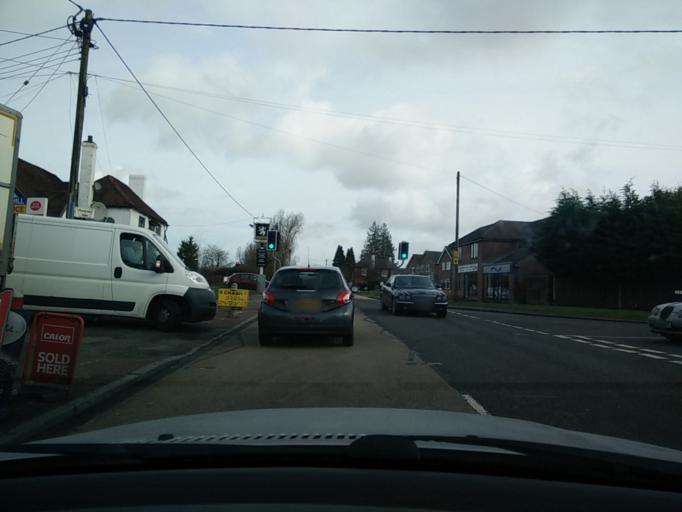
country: GB
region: England
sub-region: Buckinghamshire
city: High Wycombe
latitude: 51.6645
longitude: -0.7363
